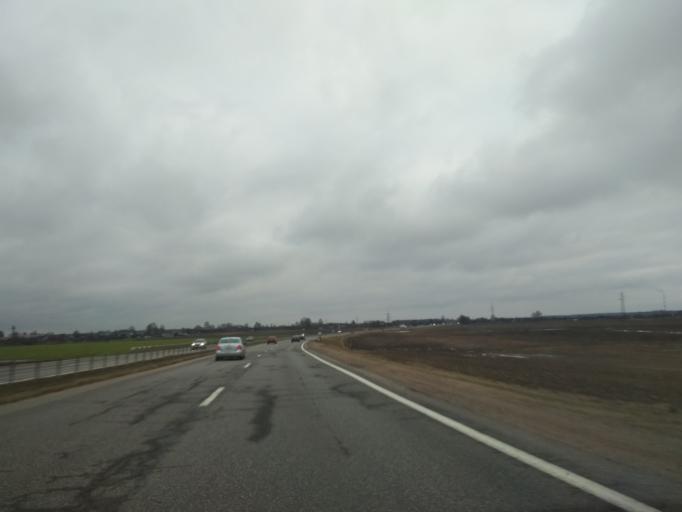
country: BY
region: Minsk
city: Dukora
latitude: 53.6777
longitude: 27.9272
